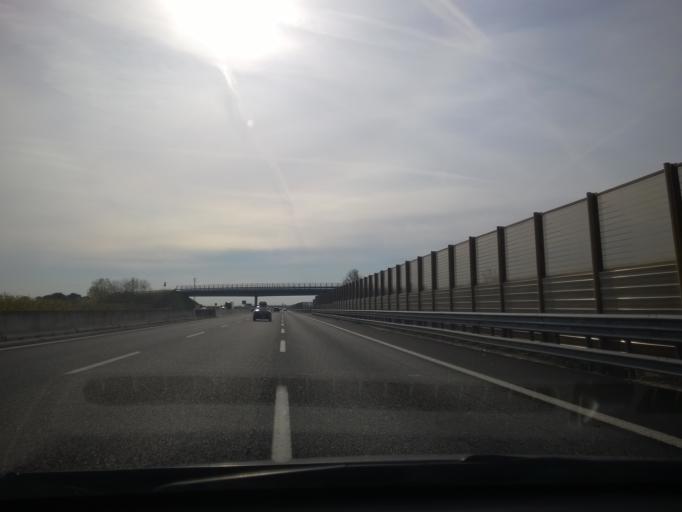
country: IT
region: Emilia-Romagna
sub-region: Forli-Cesena
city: Cesena
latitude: 44.1867
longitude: 12.2456
